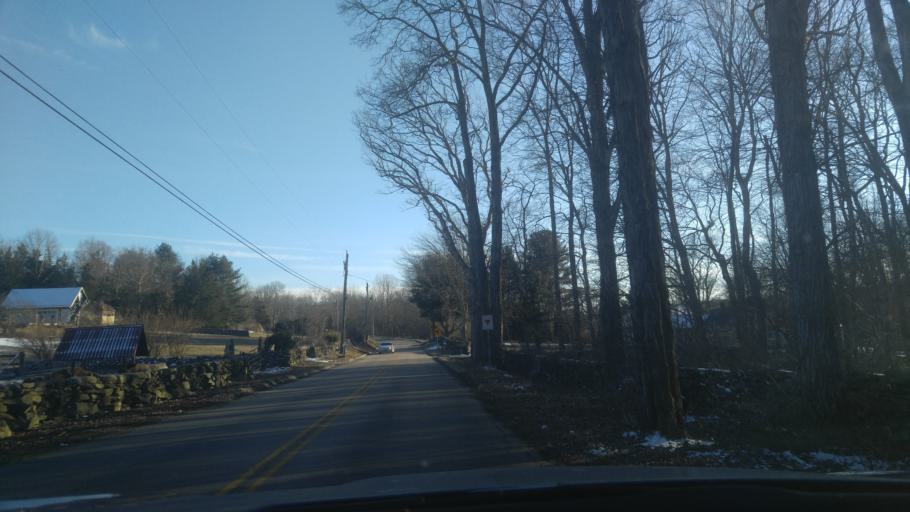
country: US
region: Connecticut
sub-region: New London County
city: Ledyard Center
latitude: 41.4840
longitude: -72.0083
